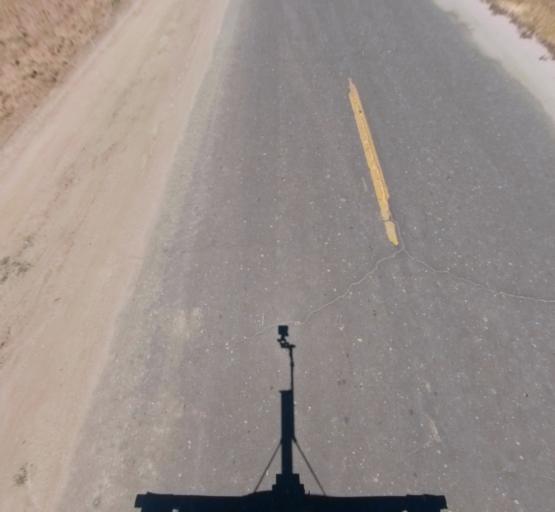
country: US
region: California
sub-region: Madera County
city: Madera
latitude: 36.9814
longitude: -120.0771
